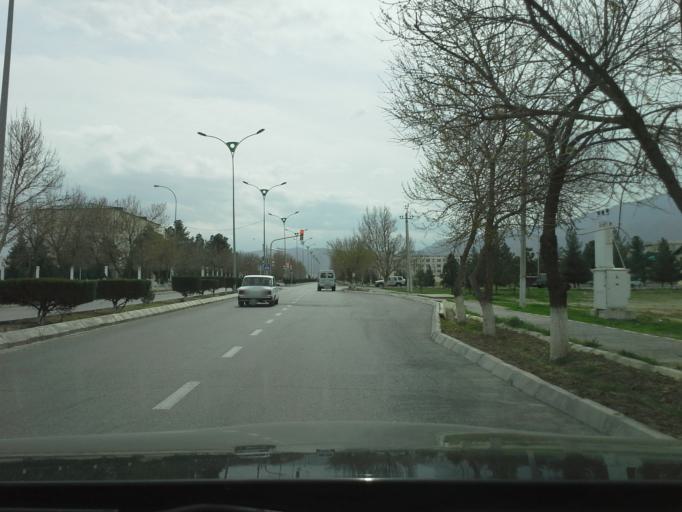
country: TM
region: Ahal
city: Abadan
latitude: 38.0576
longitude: 58.1580
